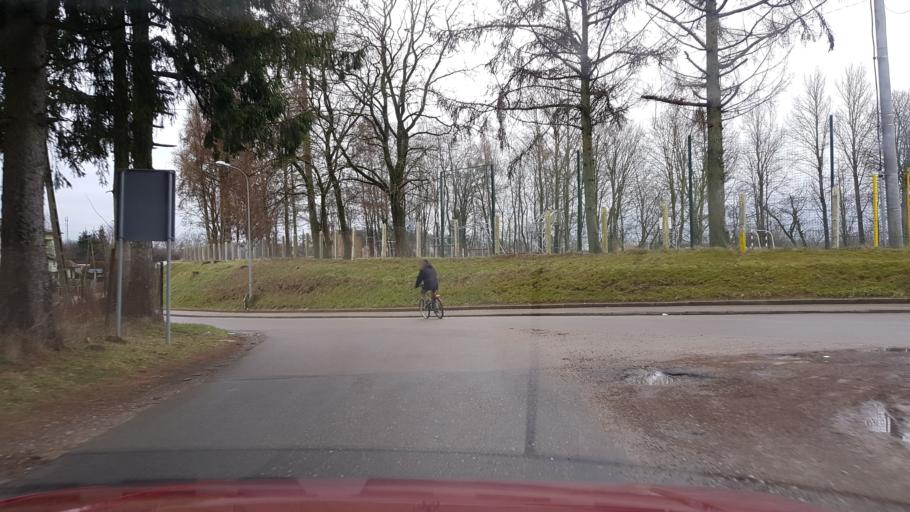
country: PL
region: West Pomeranian Voivodeship
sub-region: Powiat koszalinski
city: Mielno
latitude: 54.1377
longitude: 16.0363
